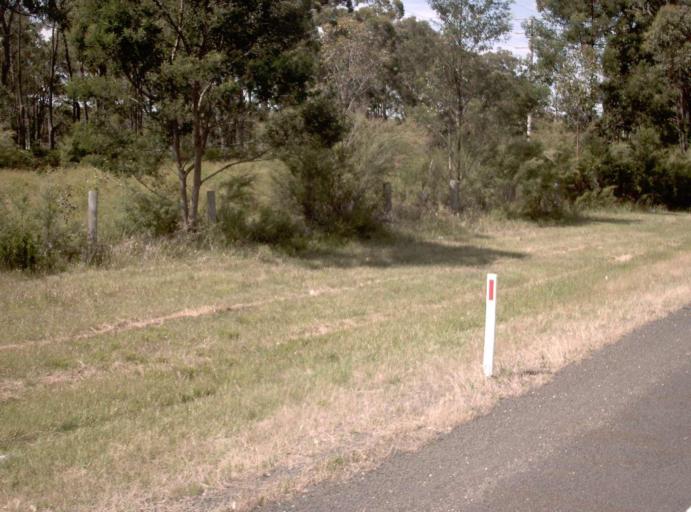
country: AU
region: Victoria
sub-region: East Gippsland
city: Bairnsdale
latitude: -37.9113
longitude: 147.3125
